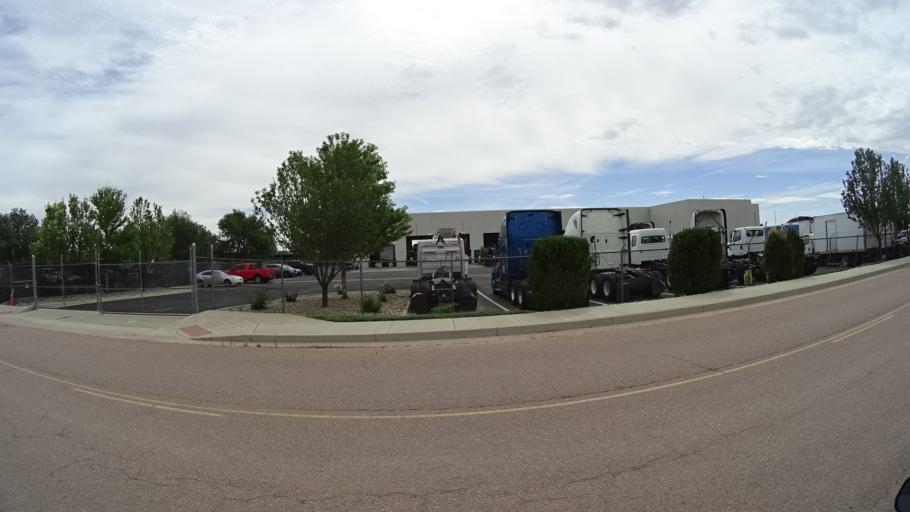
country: US
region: Colorado
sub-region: El Paso County
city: Fountain
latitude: 38.6742
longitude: -104.7150
